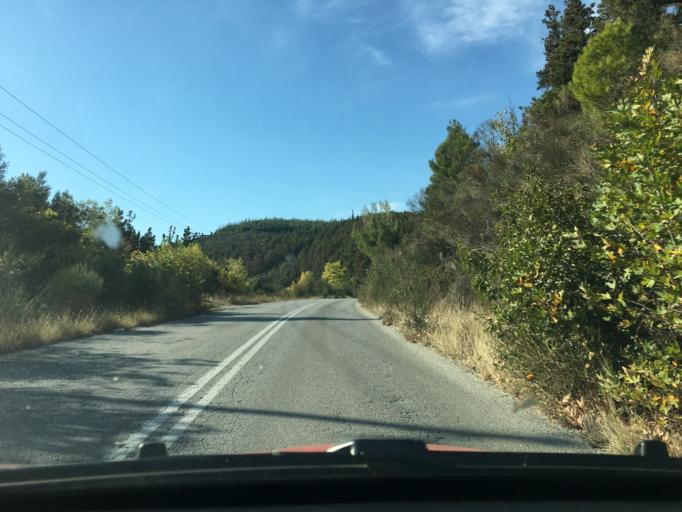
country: GR
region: Central Macedonia
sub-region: Nomos Chalkidikis
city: Megali Panagia
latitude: 40.3864
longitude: 23.7629
